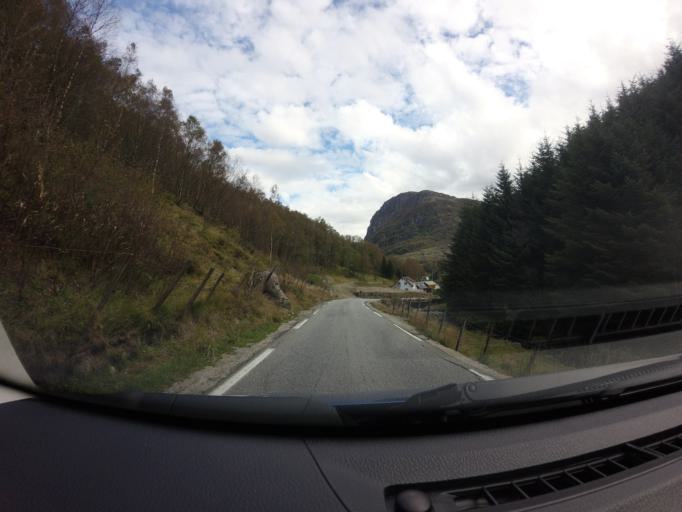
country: NO
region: Rogaland
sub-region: Forsand
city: Forsand
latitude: 58.7789
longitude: 6.3123
